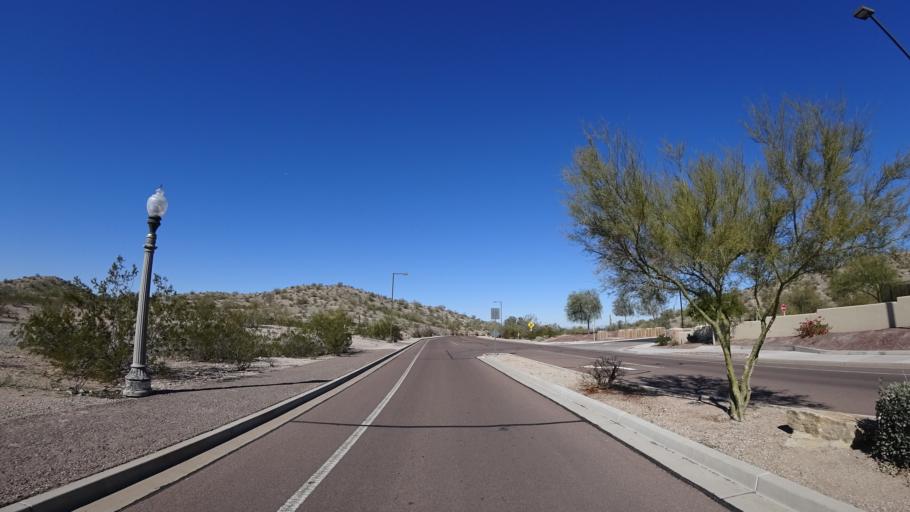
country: US
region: Arizona
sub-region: Maricopa County
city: Goodyear
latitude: 33.3574
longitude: -112.4308
